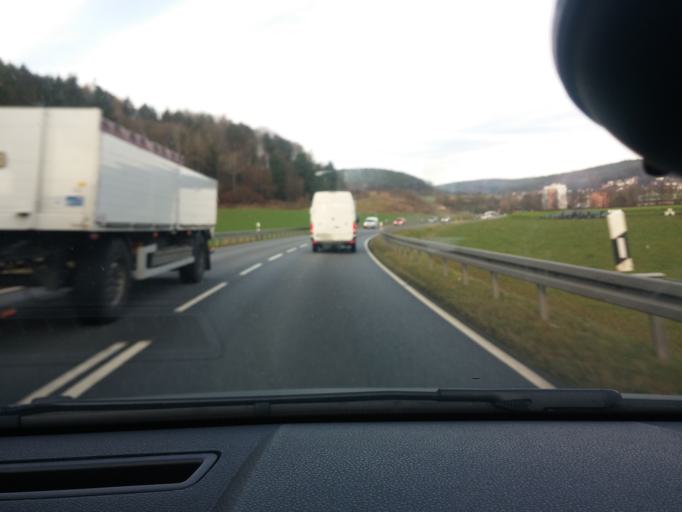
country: DE
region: Hesse
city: Hochst im Odenwald
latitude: 49.7858
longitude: 8.9904
